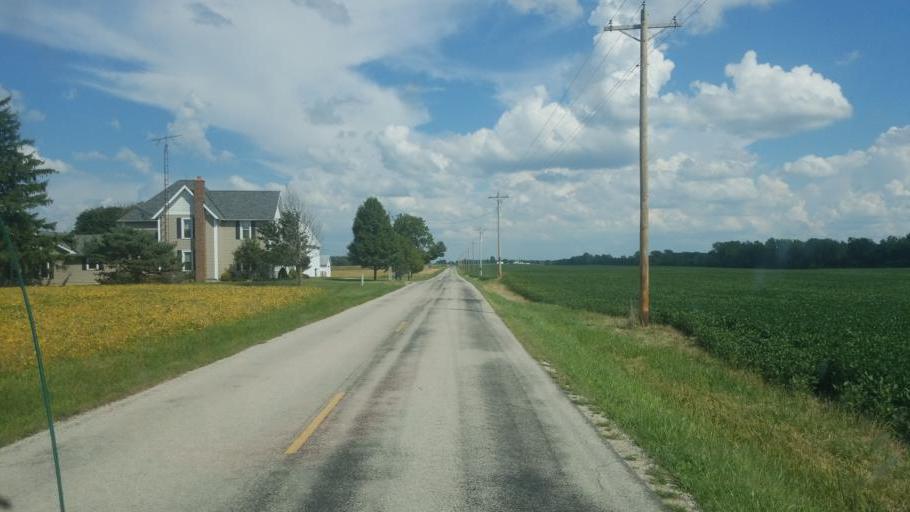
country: US
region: Ohio
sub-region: Seneca County
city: Tiffin
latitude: 40.9935
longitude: -83.0932
